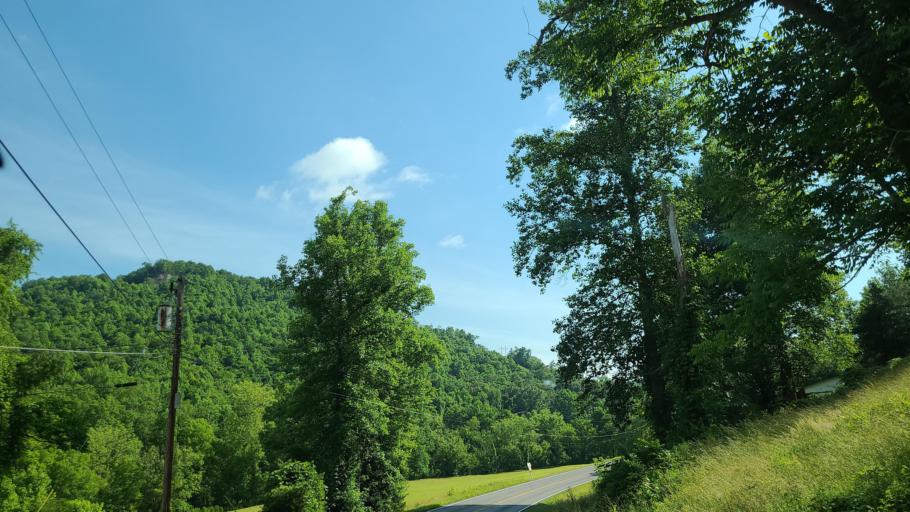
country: US
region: Kentucky
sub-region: Bell County
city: Pineville
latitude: 36.7844
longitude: -83.7678
